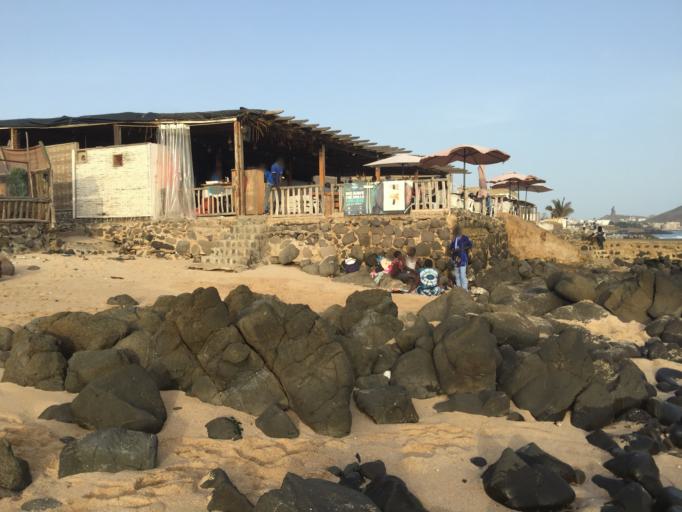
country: SN
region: Dakar
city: Mermoz Boabab
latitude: 14.7406
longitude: -17.5206
